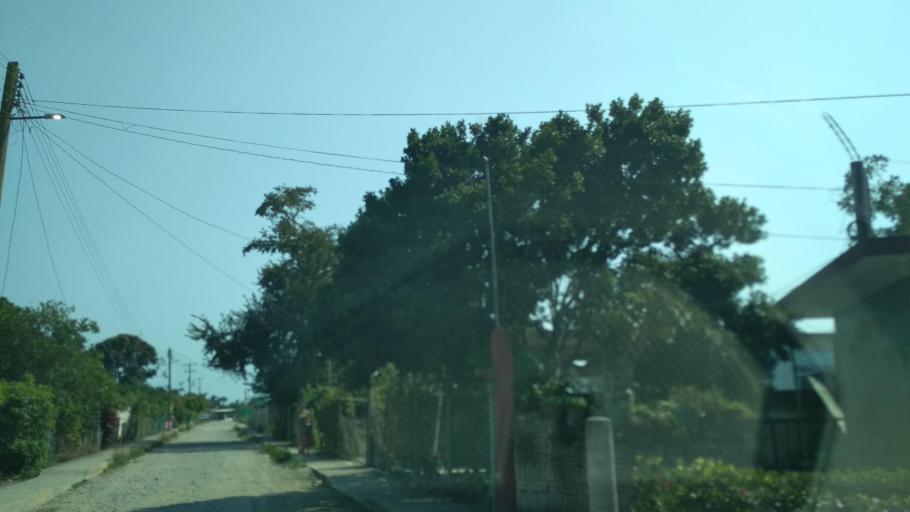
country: MX
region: Veracruz
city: Gutierrez Zamora
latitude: 20.4218
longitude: -97.1889
